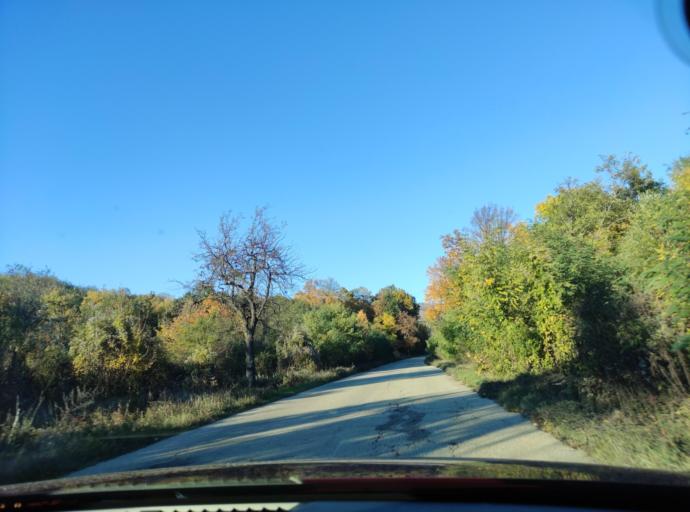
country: BG
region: Montana
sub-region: Obshtina Chiprovtsi
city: Chiprovtsi
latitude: 43.4232
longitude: 22.9559
